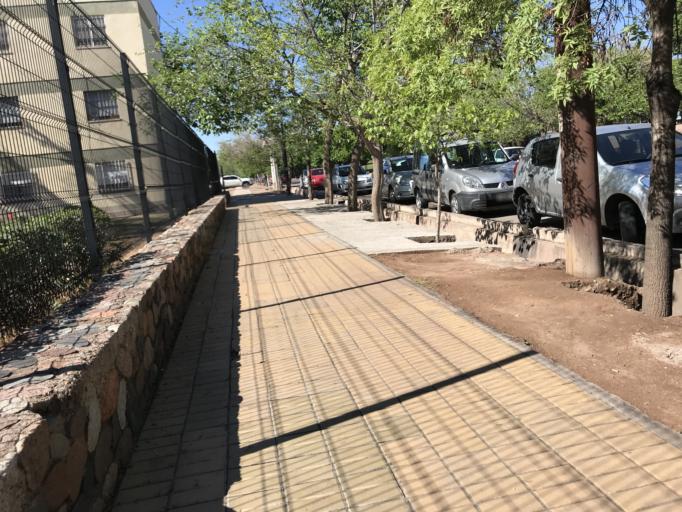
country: AR
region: Mendoza
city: Mendoza
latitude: -32.8765
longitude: -68.8383
